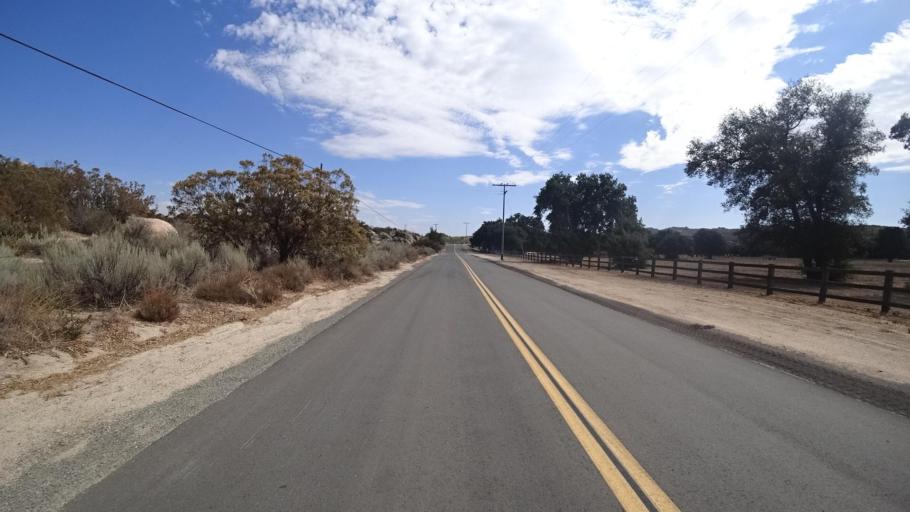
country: MX
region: Baja California
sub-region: Tecate
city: Cereso del Hongo
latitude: 32.6497
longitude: -116.2903
